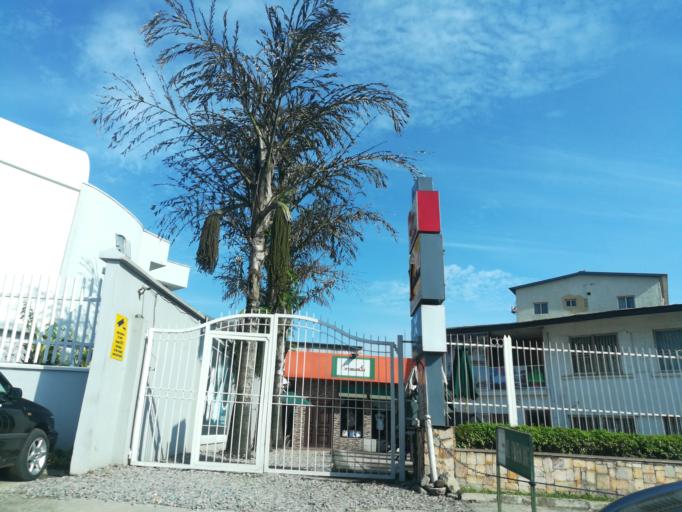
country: NG
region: Lagos
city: Ikeja
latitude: 6.6071
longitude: 3.3406
